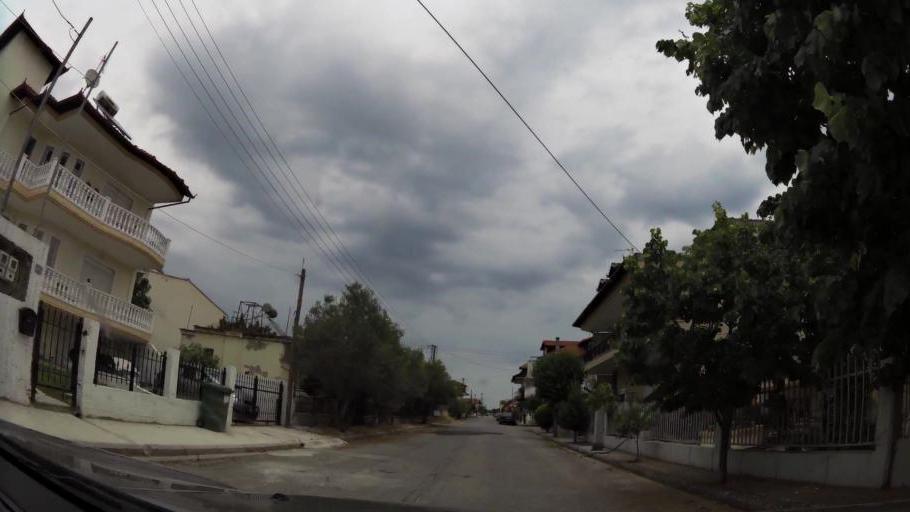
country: GR
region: Central Macedonia
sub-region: Nomos Pierias
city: Kallithea
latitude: 40.2718
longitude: 22.5780
